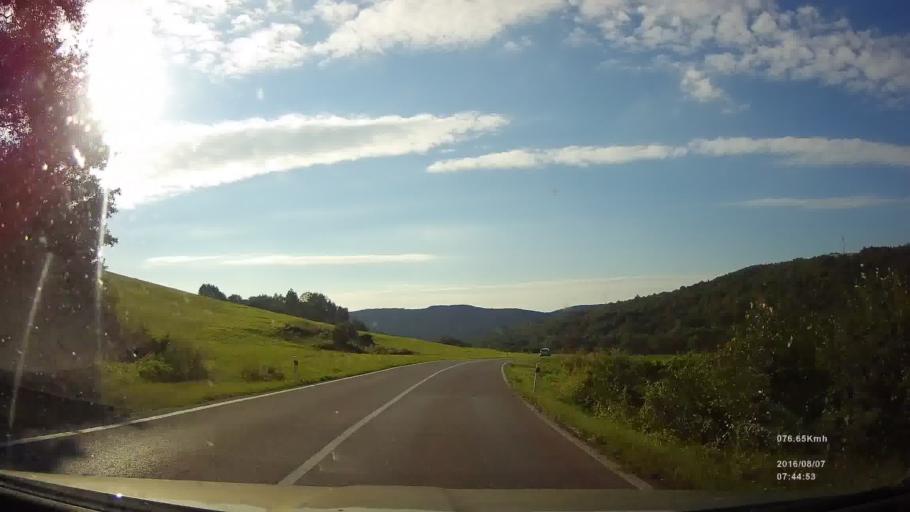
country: SK
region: Presovsky
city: Stropkov
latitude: 49.2648
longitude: 21.7334
